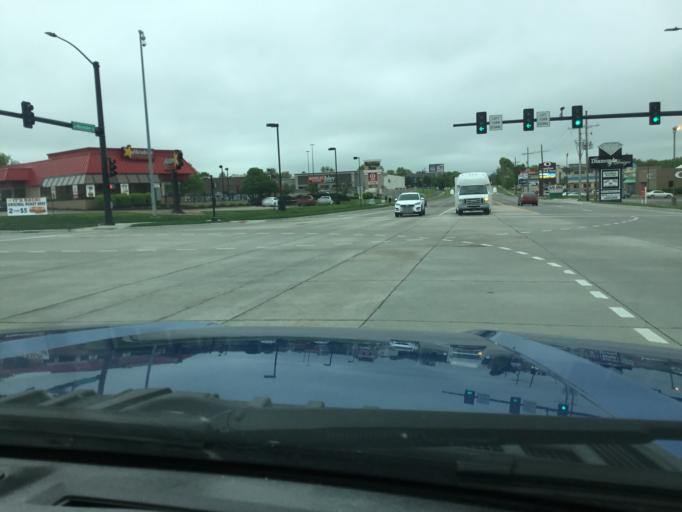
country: US
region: Kansas
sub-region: Shawnee County
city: Topeka
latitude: 39.0293
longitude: -95.7622
